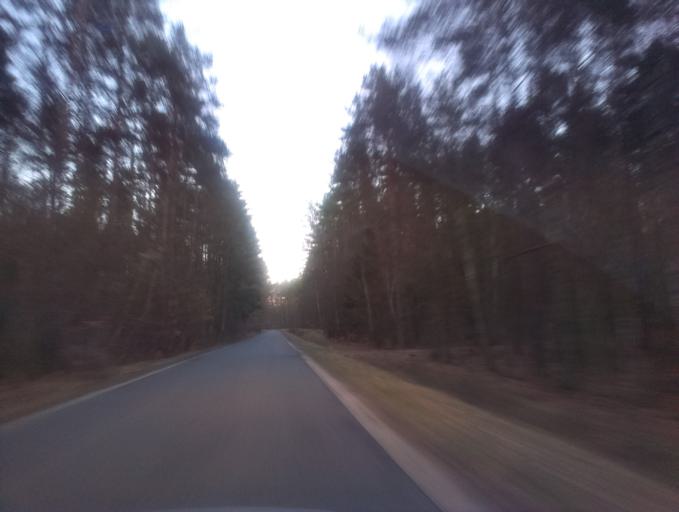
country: PL
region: Greater Poland Voivodeship
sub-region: Powiat zlotowski
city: Okonek
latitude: 53.5325
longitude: 16.9233
